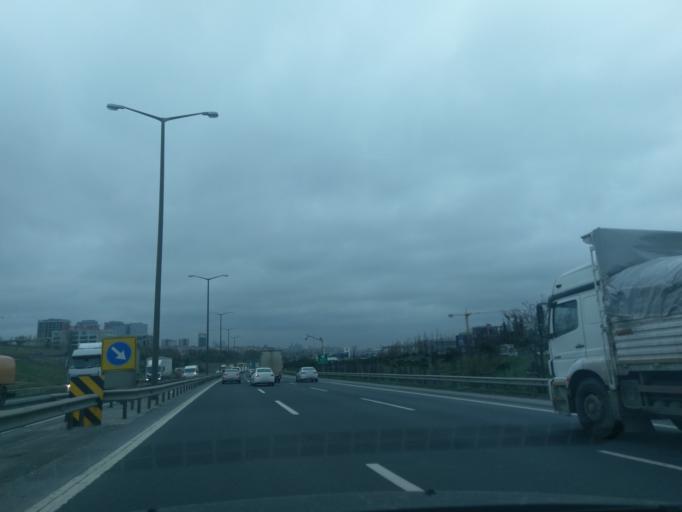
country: TR
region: Istanbul
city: Esenyurt
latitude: 41.0768
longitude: 28.6451
